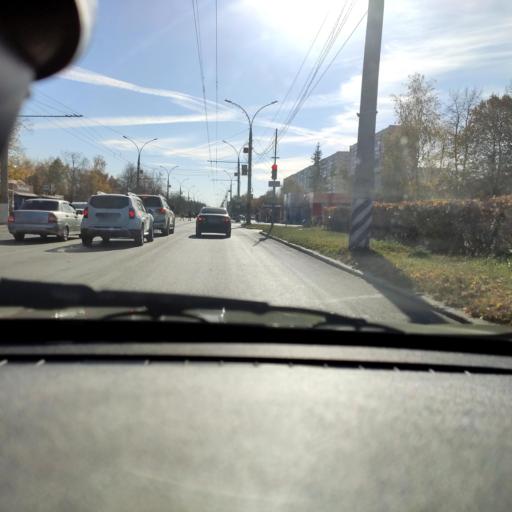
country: RU
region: Samara
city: Tol'yatti
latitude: 53.5276
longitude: 49.2758
